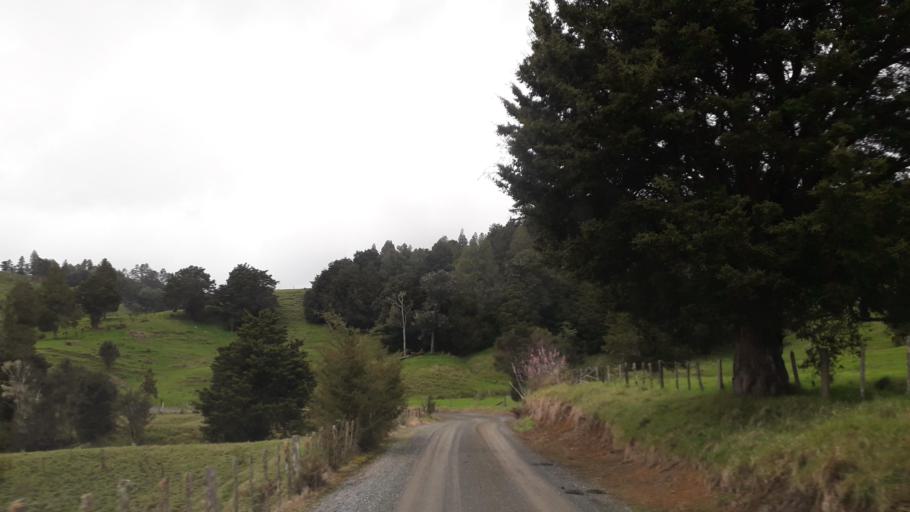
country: NZ
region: Northland
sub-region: Far North District
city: Waimate North
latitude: -35.1551
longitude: 173.7150
